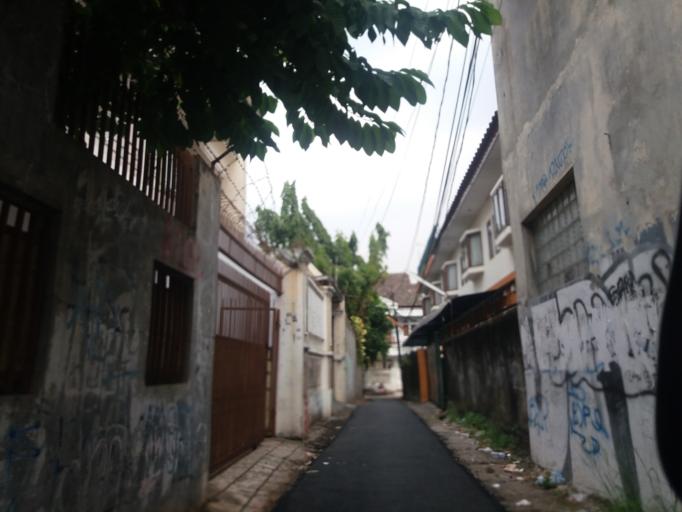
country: ID
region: Jakarta Raya
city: Jakarta
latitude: -6.1901
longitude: 106.8192
